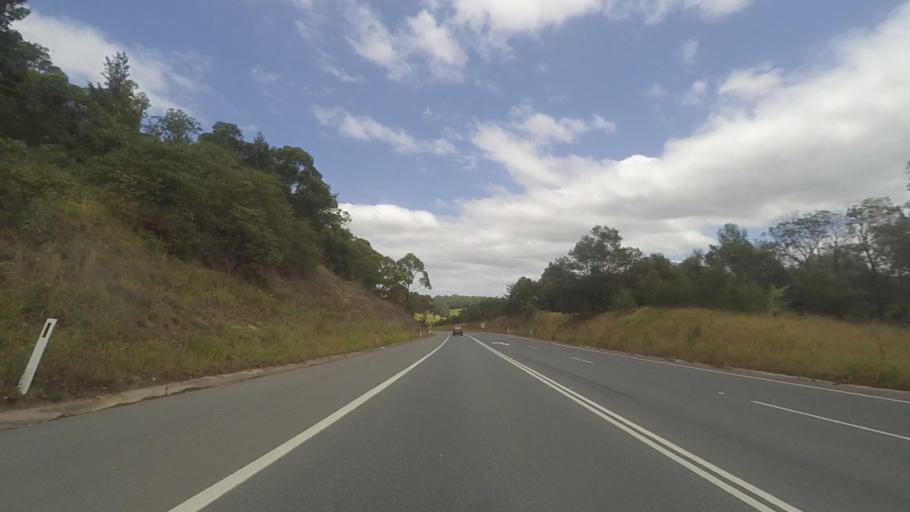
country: AU
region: New South Wales
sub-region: Shoalhaven Shire
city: Milton
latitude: -35.2634
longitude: 150.4266
